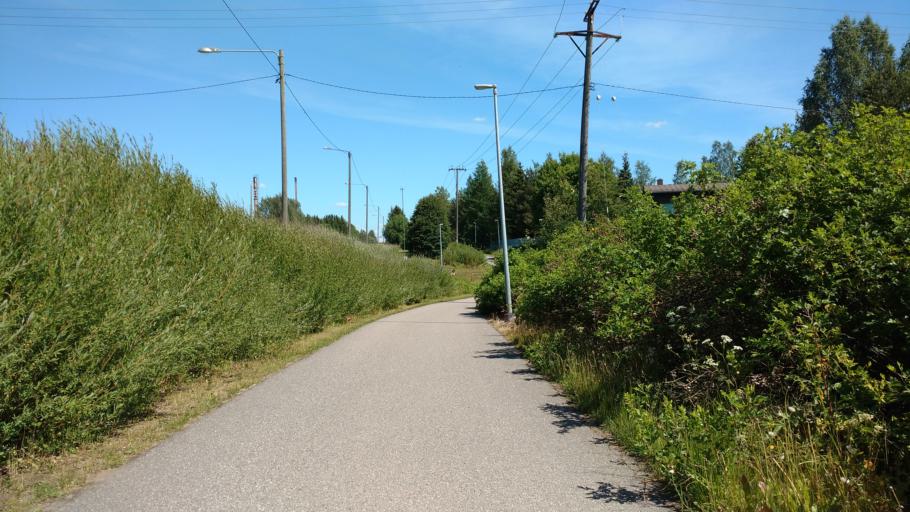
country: FI
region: Varsinais-Suomi
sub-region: Salo
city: Salo
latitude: 60.3972
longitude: 23.1379
